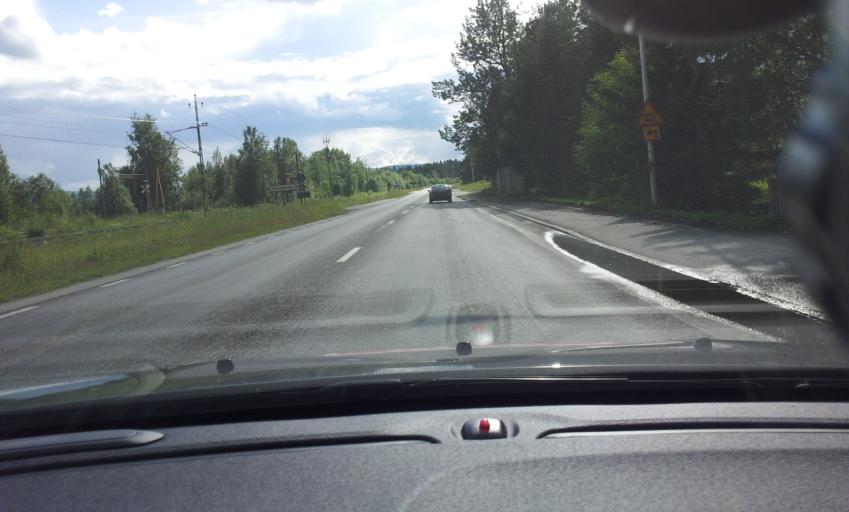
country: SE
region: Jaemtland
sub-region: Are Kommun
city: Jarpen
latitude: 63.3422
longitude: 13.4488
